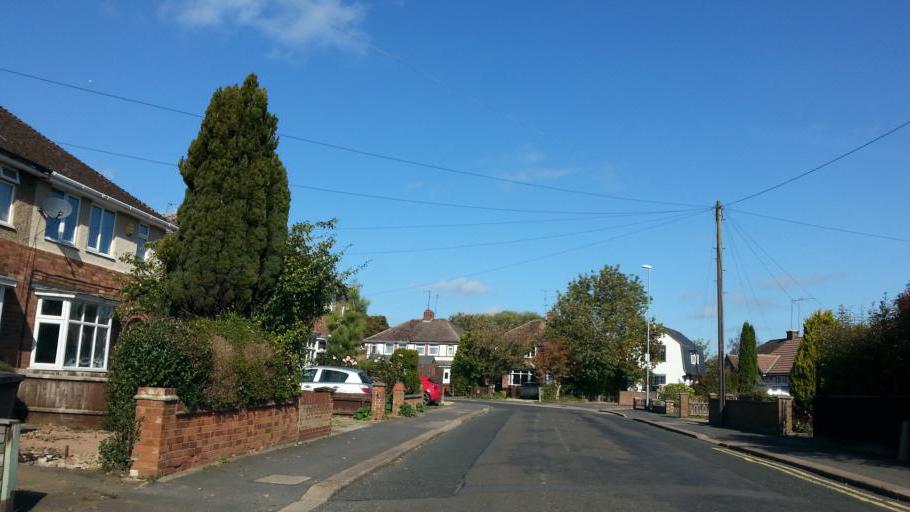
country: GB
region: England
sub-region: Northamptonshire
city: Rushden
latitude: 52.2821
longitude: -0.6002
